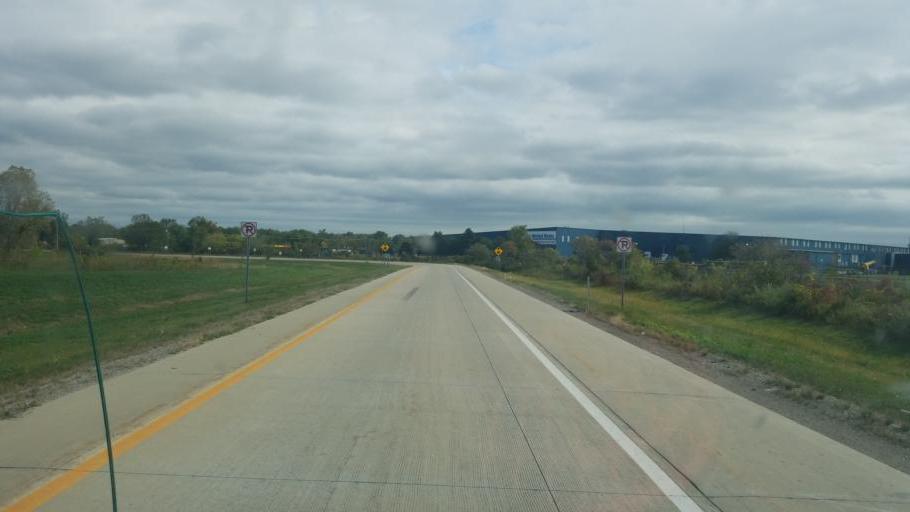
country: US
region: Michigan
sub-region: Monroe County
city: Detroit Beach
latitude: 41.9623
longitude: -83.3503
